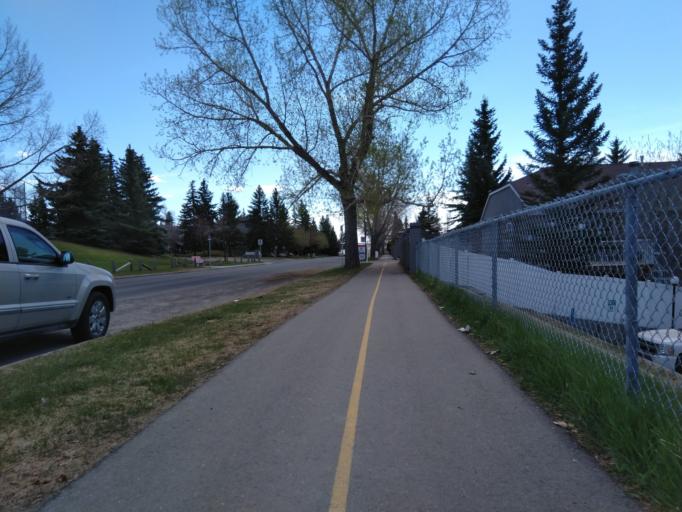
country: CA
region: Alberta
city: Calgary
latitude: 51.0132
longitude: -114.1599
